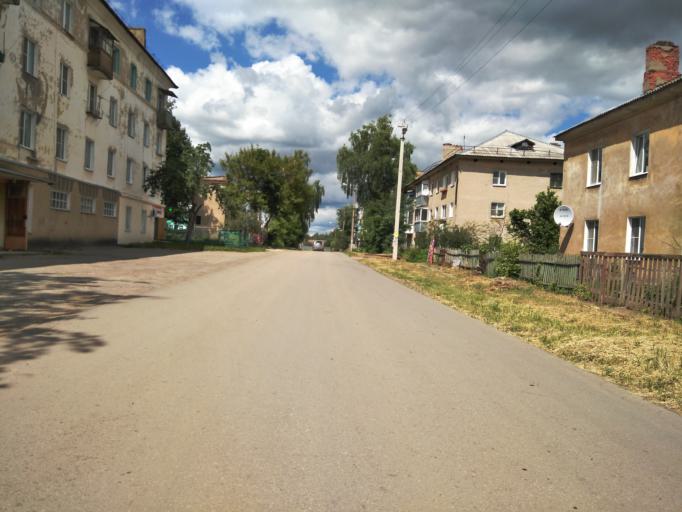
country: RU
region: Tula
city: Lomintsevskiy
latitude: 53.9367
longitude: 37.6277
